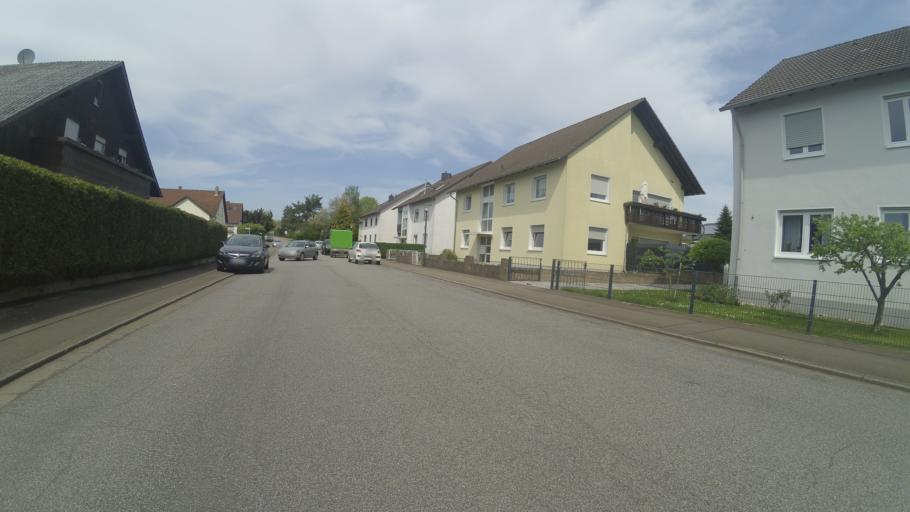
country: DE
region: Saarland
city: Homburg
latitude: 49.3488
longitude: 7.3252
